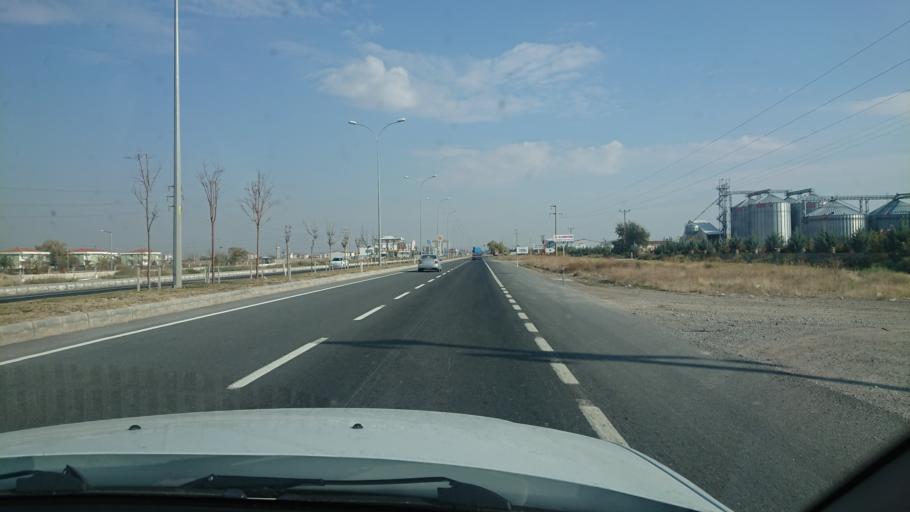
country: TR
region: Aksaray
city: Aksaray
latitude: 38.3450
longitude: 33.9532
